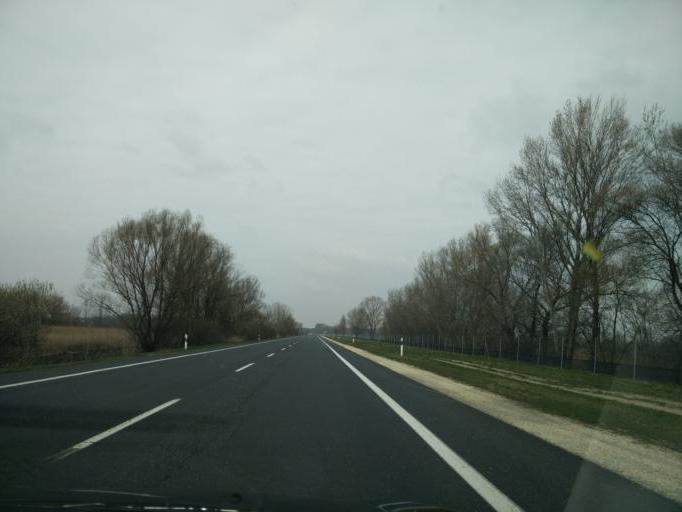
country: HU
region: Gyor-Moson-Sopron
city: Toltestava
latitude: 47.7009
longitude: 17.7690
